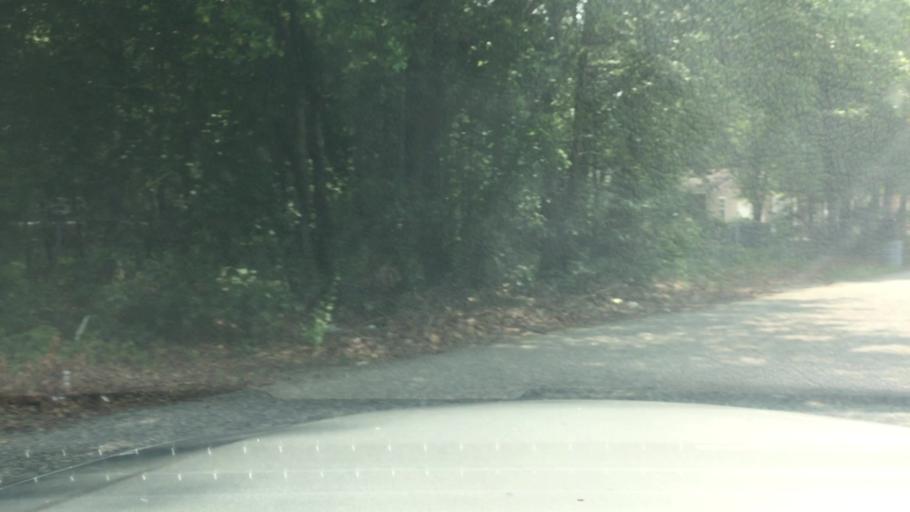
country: US
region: North Carolina
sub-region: Cumberland County
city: Fayetteville
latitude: 35.0371
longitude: -78.9422
